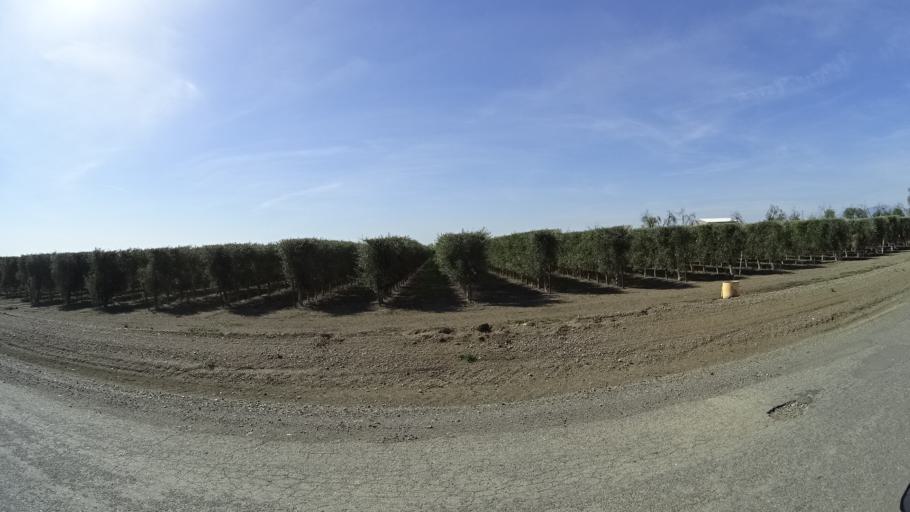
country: US
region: California
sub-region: Glenn County
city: Willows
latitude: 39.6117
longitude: -122.2566
